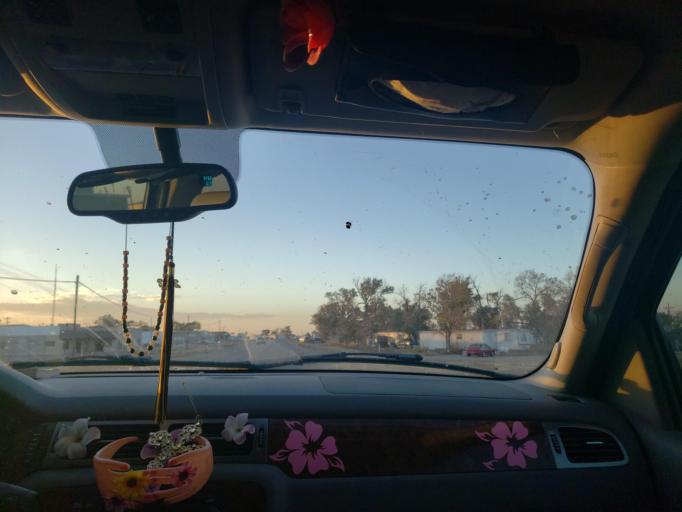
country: US
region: Kansas
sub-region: Finney County
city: Garden City
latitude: 37.9862
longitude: -100.9114
